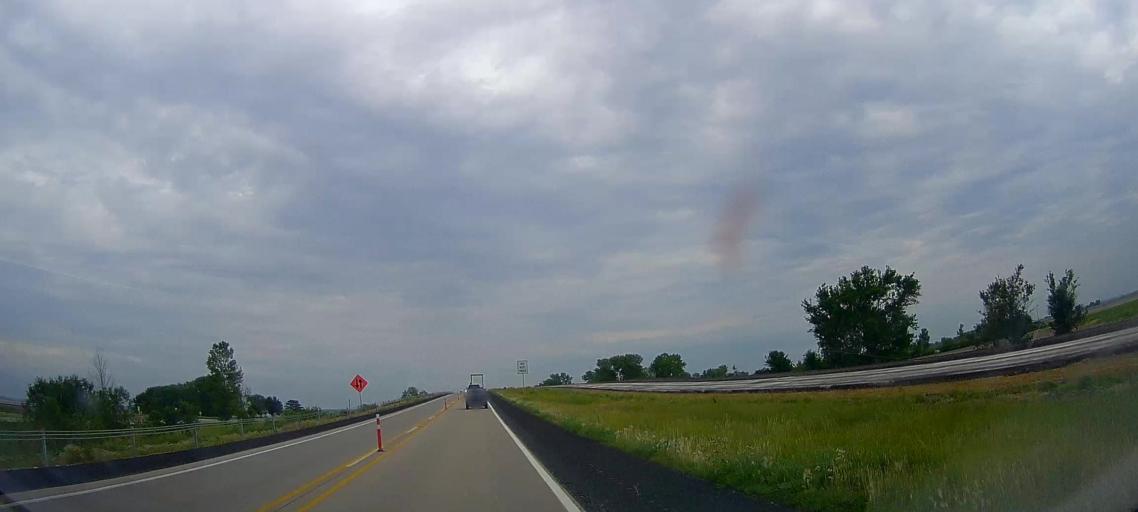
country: US
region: Nebraska
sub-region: Washington County
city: Blair
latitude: 41.6422
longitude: -96.0161
